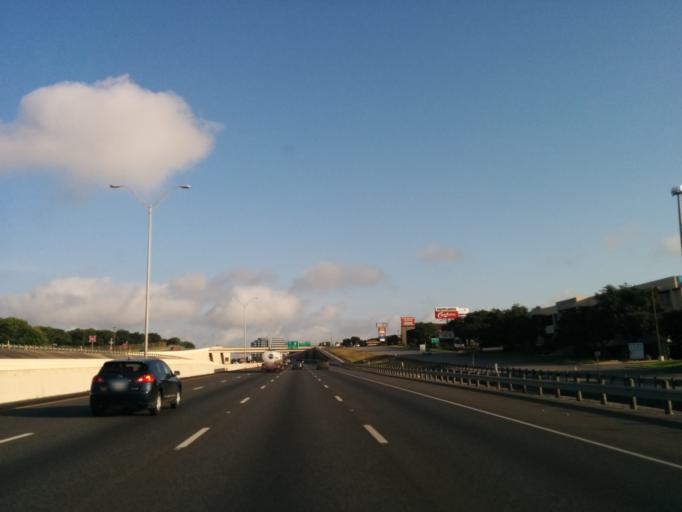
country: US
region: Texas
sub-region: Bexar County
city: Shavano Park
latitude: 29.5373
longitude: -98.5684
